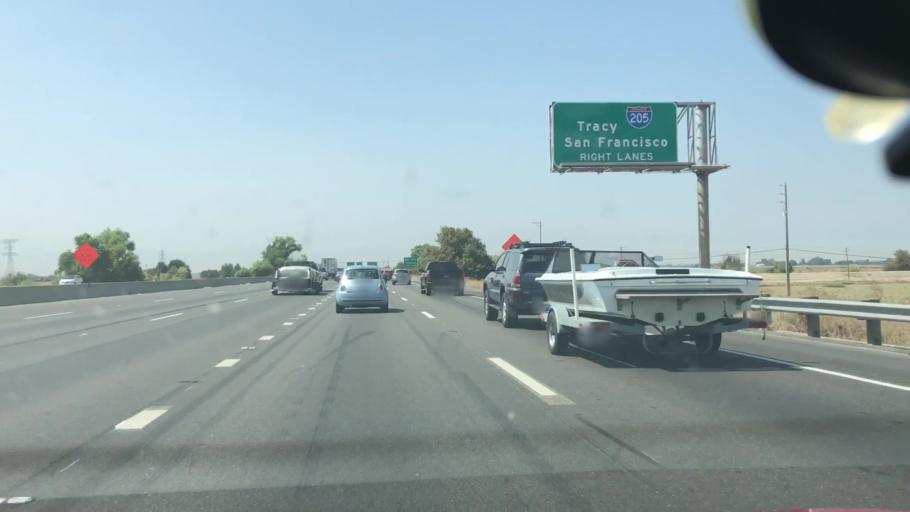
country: US
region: California
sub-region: San Joaquin County
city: Lathrop
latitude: 37.7731
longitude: -121.3244
